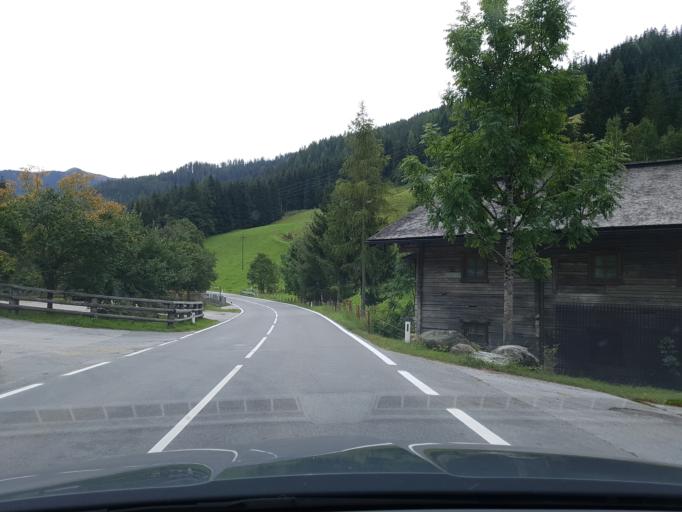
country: AT
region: Salzburg
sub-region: Politischer Bezirk Sankt Johann im Pongau
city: Forstau
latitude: 47.3769
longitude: 13.5269
